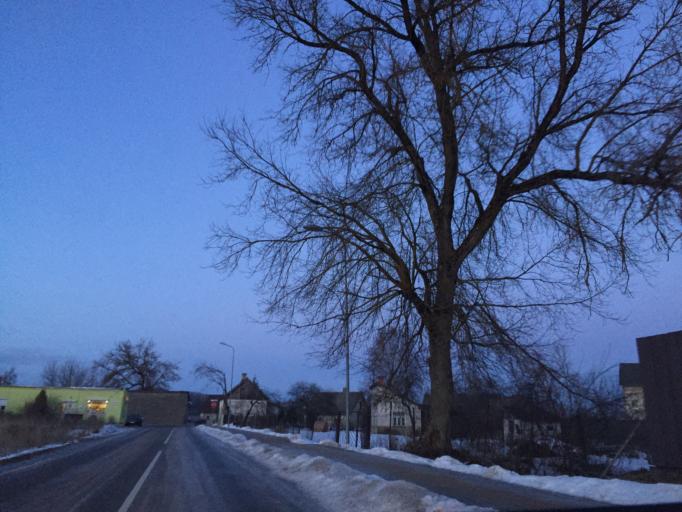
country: LV
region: Jaunjelgava
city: Jaunjelgava
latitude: 56.6183
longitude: 25.0889
